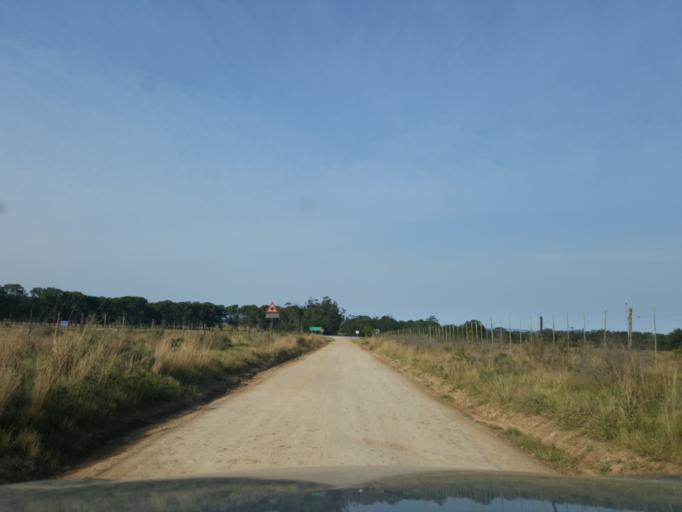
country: ZA
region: Eastern Cape
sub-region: Cacadu District Municipality
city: Grahamstown
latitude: -33.4293
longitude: 26.3210
